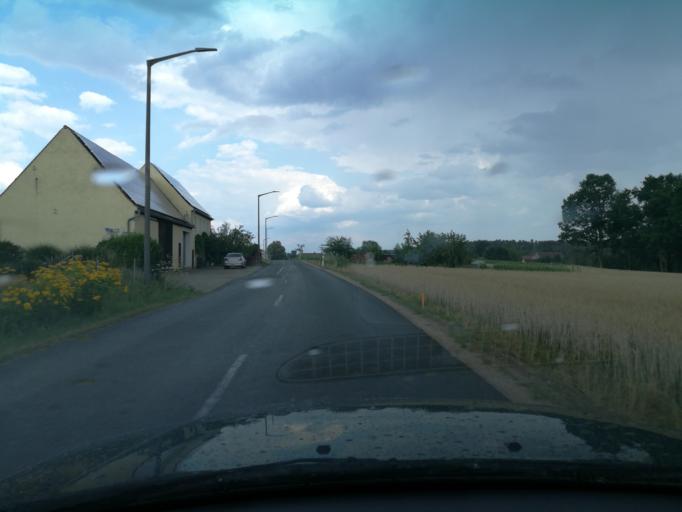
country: DE
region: Bavaria
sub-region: Regierungsbezirk Mittelfranken
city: Langenzenn
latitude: 49.4649
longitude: 10.7954
